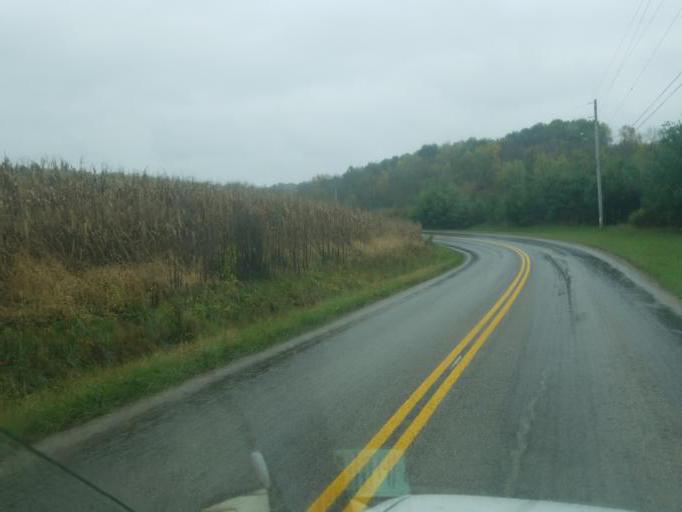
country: US
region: Ohio
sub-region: Holmes County
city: Millersburg
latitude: 40.6265
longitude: -81.9370
